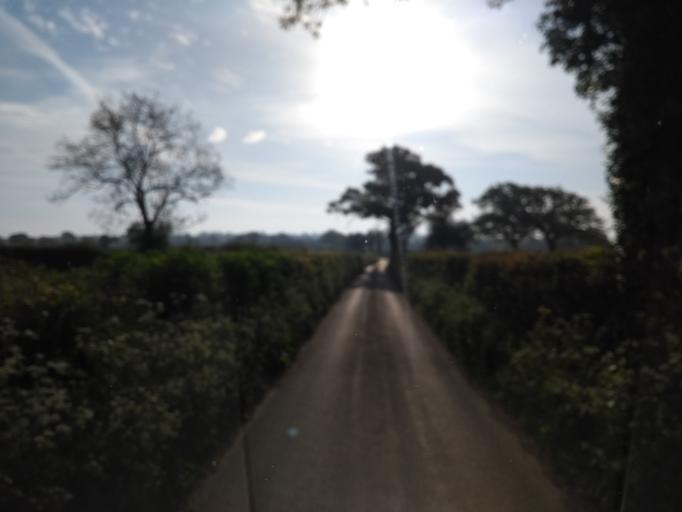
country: GB
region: England
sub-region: Devon
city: Axminster
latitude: 50.8172
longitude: -2.9531
